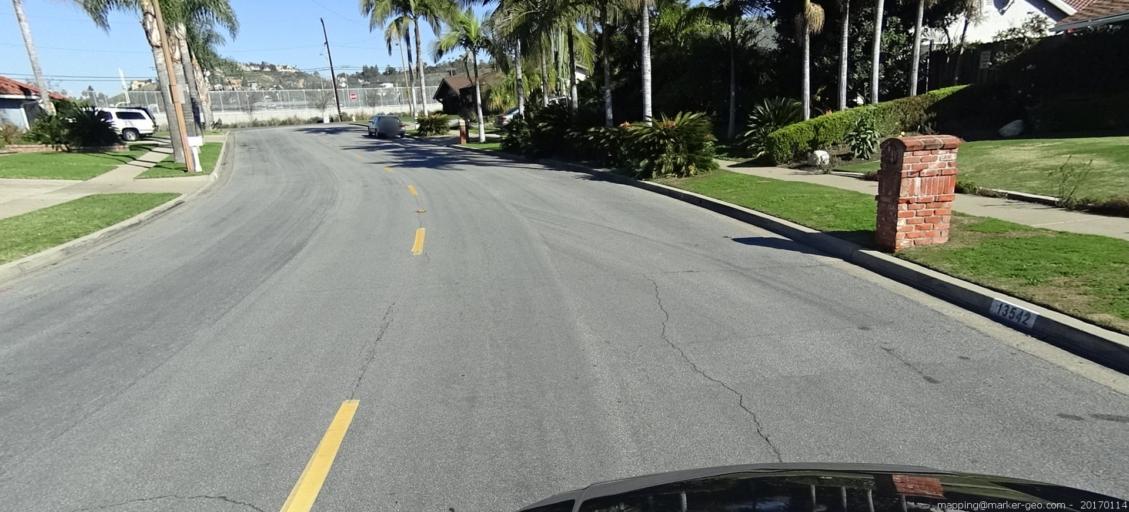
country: US
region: California
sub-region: Orange County
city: North Tustin
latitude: 33.7651
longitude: -117.8013
